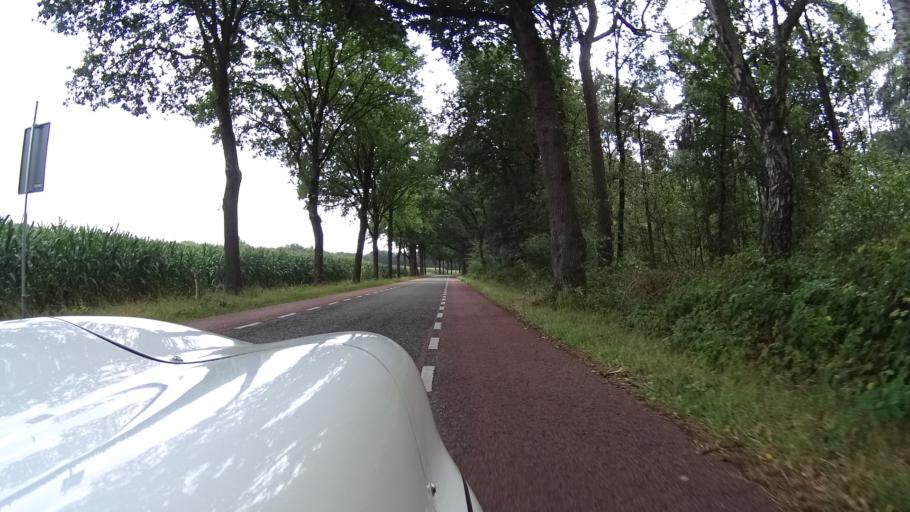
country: NL
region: North Brabant
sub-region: Gemeente Bernheze
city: Loosbroek
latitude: 51.6778
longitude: 5.4631
